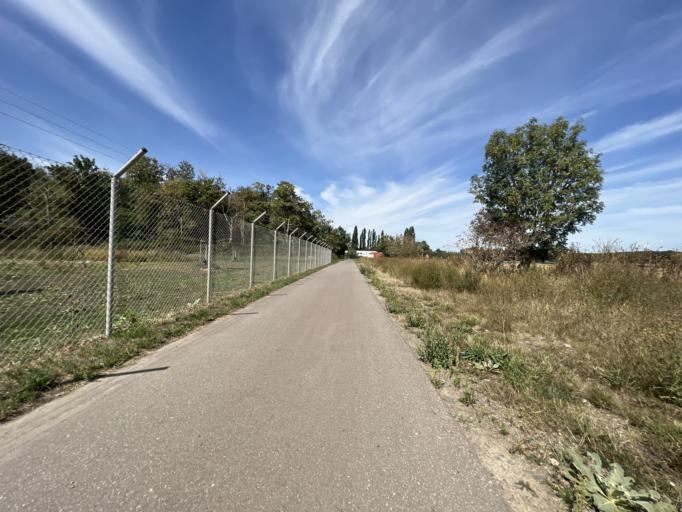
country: DE
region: North Rhine-Westphalia
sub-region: Regierungsbezirk Koln
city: Niederzier
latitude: 50.8463
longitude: 6.4349
